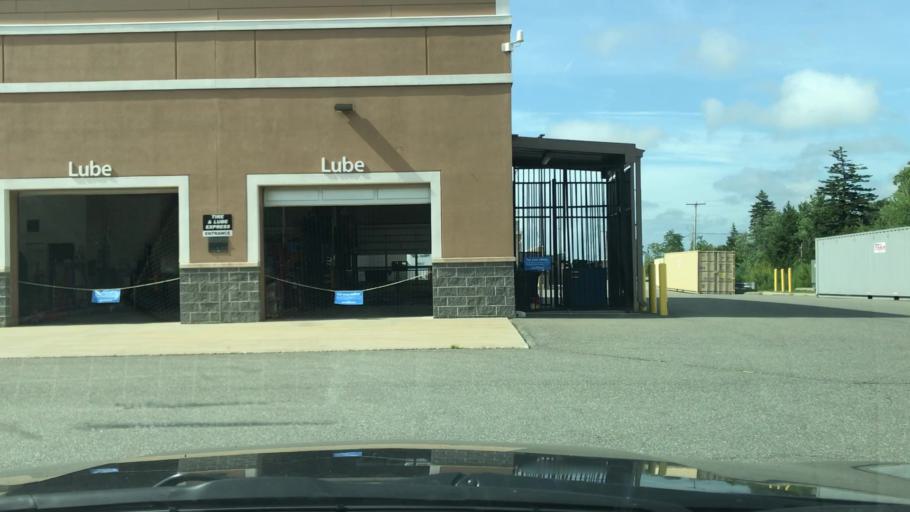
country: US
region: Maine
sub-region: Hancock County
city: Ellsworth
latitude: 44.5239
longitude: -68.3919
